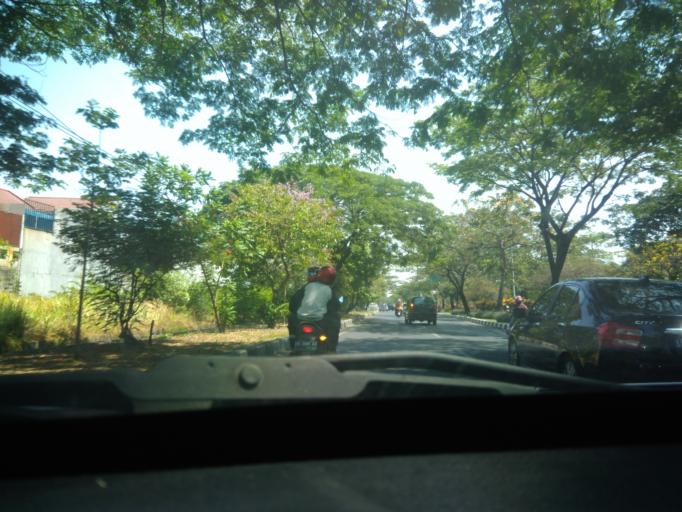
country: ID
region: East Java
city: Semampir
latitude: -7.3026
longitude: 112.7814
